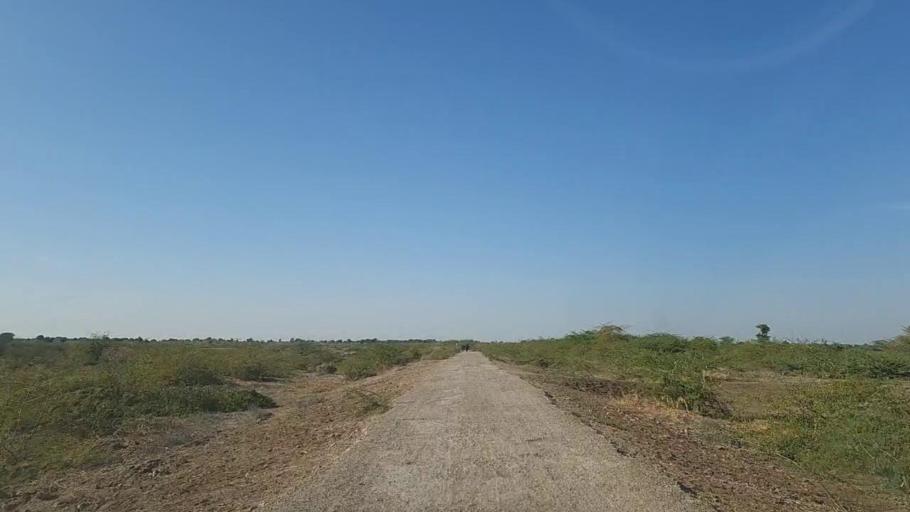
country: PK
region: Sindh
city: Samaro
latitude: 25.2522
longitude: 69.4930
